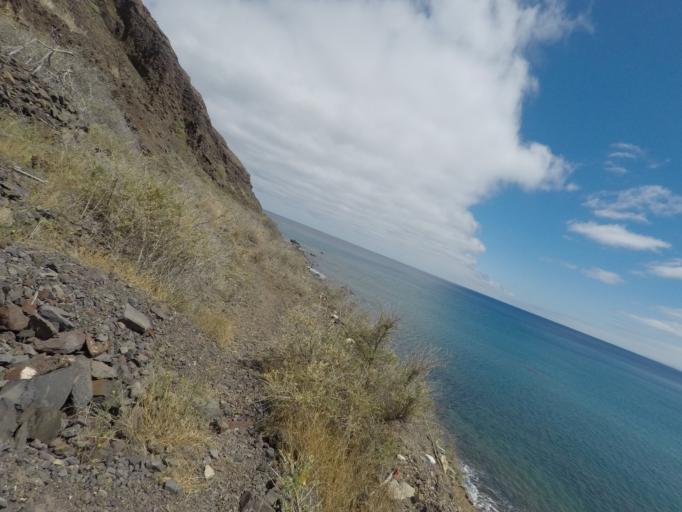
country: PT
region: Madeira
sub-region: Porto Santo
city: Vila de Porto Santo
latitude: 33.0620
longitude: -16.3021
